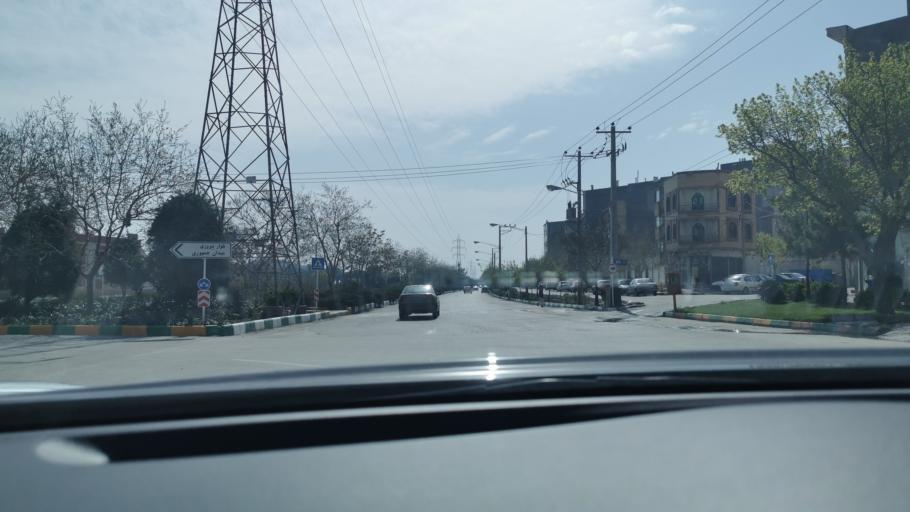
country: IR
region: Razavi Khorasan
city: Mashhad
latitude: 36.2829
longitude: 59.5442
